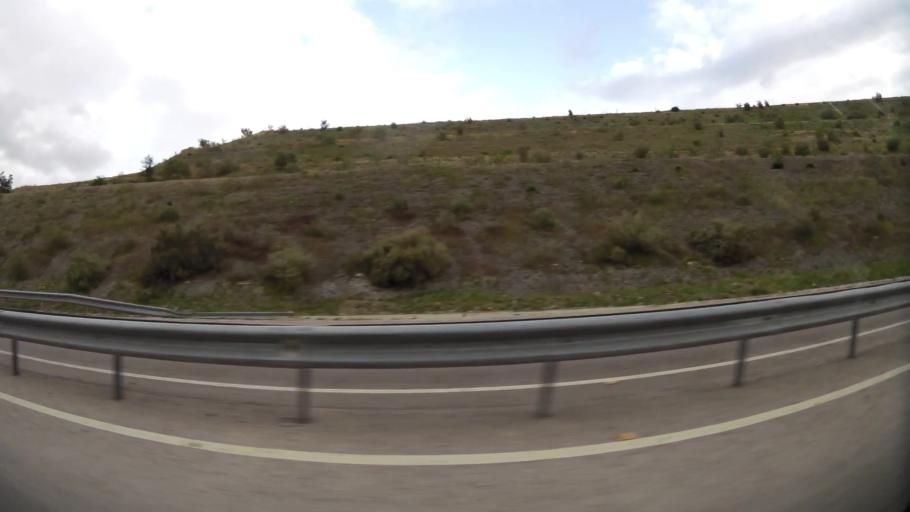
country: MA
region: Taza-Al Hoceima-Taounate
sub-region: Taza
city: Taza
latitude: 34.2593
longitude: -3.9557
